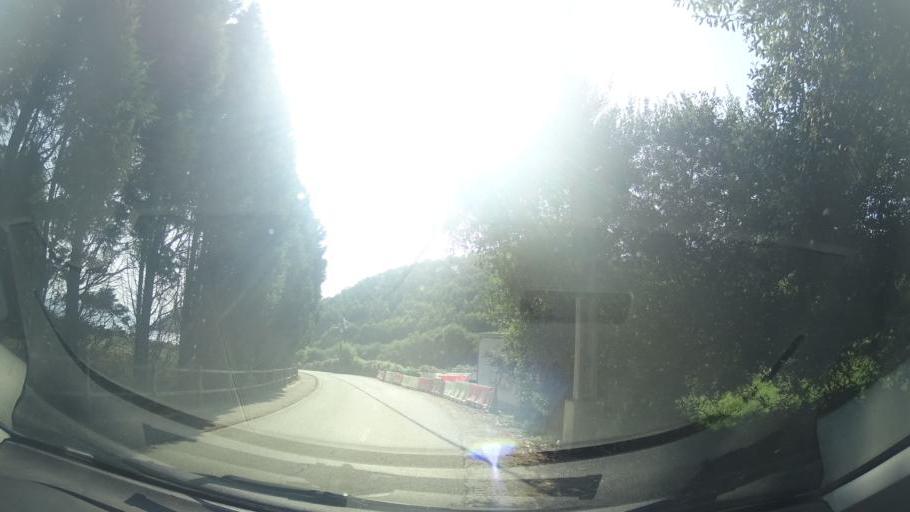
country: ES
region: Asturias
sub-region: Province of Asturias
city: Colunga
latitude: 43.4740
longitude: -5.1811
